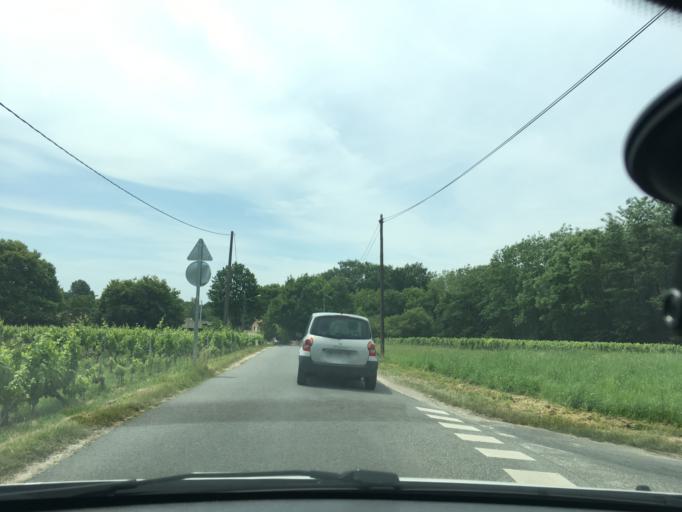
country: FR
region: Aquitaine
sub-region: Departement de la Gironde
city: Castelnau-de-Medoc
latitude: 45.0525
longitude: -0.8093
